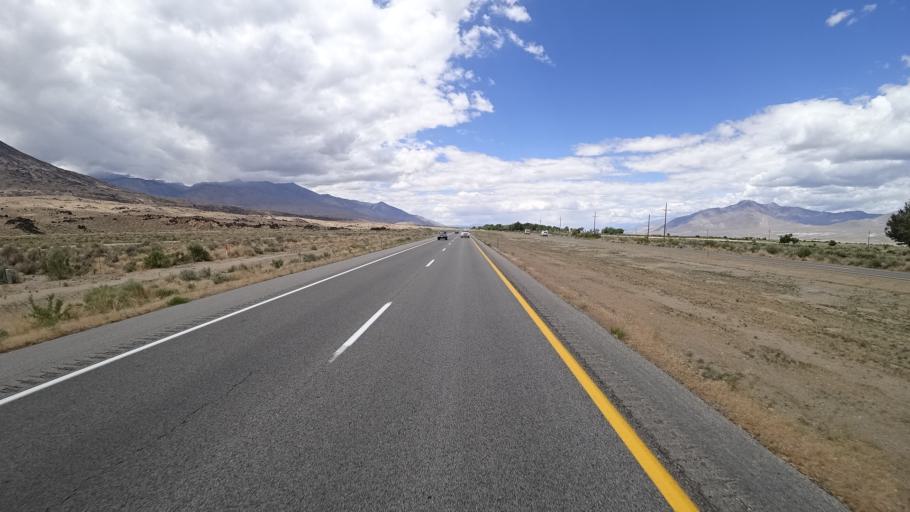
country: US
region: California
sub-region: Inyo County
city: Big Pine
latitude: 37.1177
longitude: -118.2608
